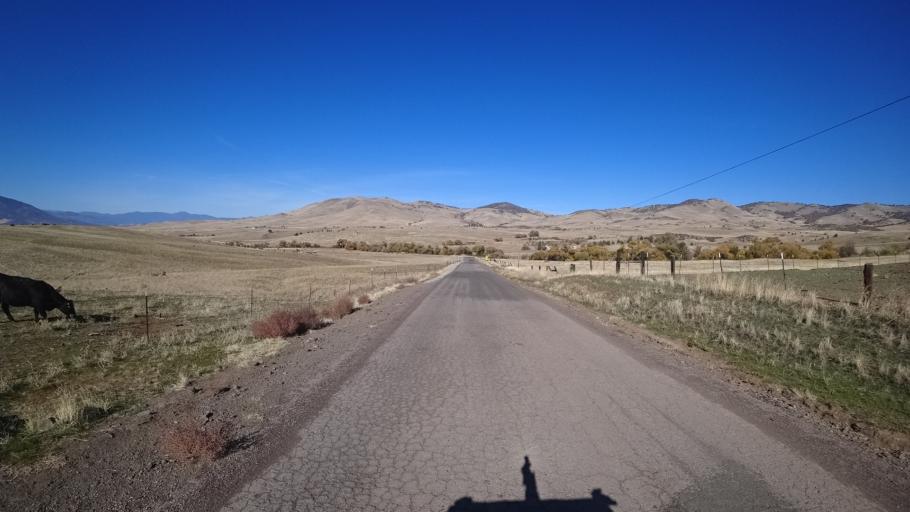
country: US
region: California
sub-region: Siskiyou County
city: Montague
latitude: 41.8119
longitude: -122.3767
